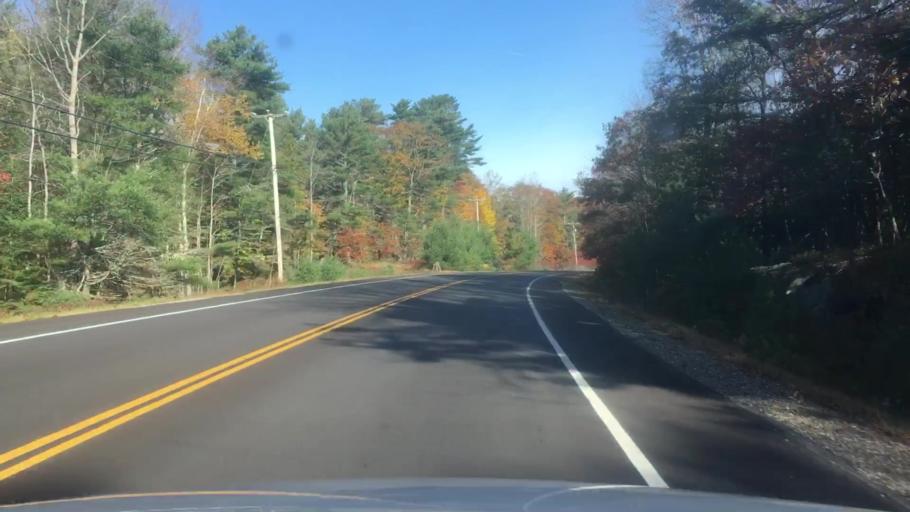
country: US
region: Maine
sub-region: Sagadahoc County
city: Woolwich
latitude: 43.8830
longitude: -69.7890
